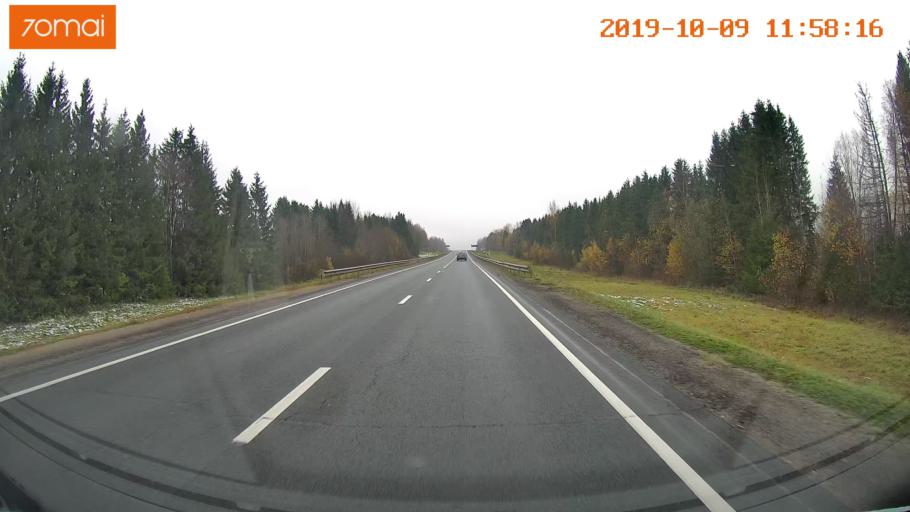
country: RU
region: Vologda
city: Gryazovets
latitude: 58.7204
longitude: 40.2963
